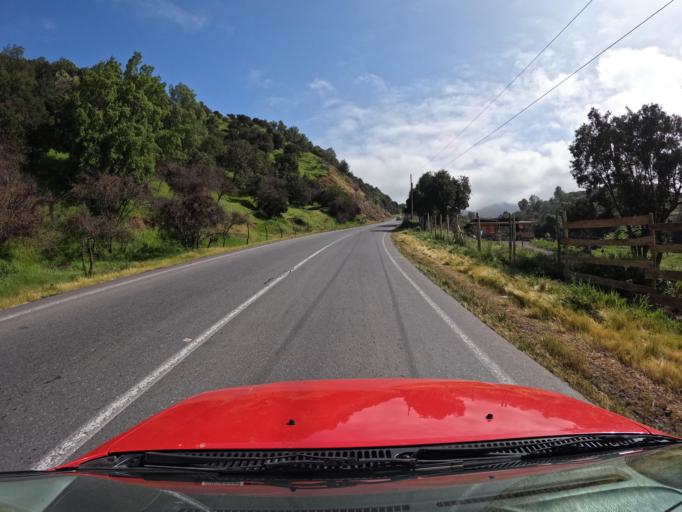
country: CL
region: Maule
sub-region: Provincia de Curico
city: Teno
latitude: -34.8235
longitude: -71.1925
